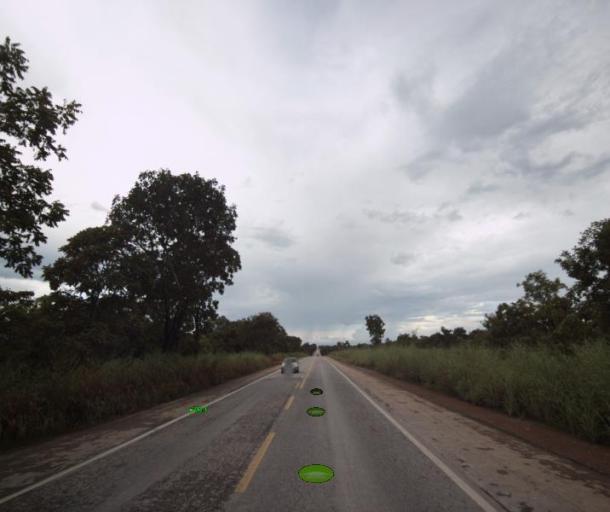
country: BR
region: Goias
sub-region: Porangatu
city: Porangatu
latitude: -13.5908
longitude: -49.0417
